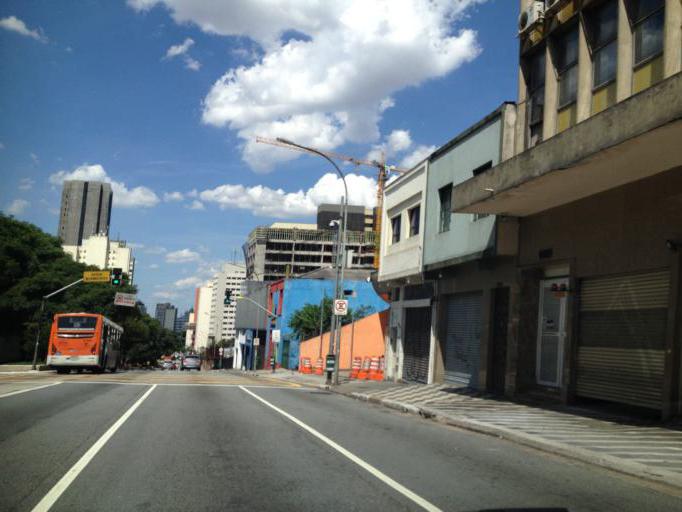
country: BR
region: Sao Paulo
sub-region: Sao Paulo
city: Sao Paulo
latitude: -23.5516
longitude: -46.6568
